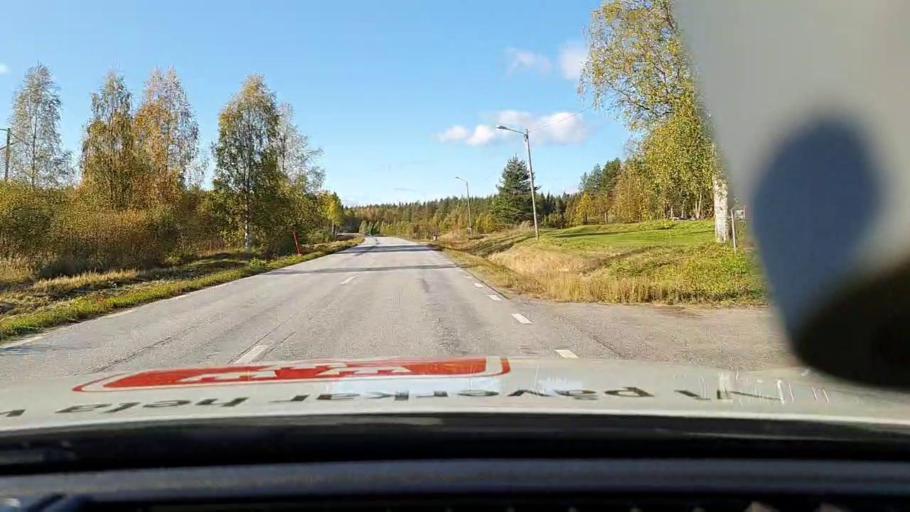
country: SE
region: Norrbotten
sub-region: Pitea Kommun
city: Norrfjarden
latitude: 65.4317
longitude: 21.4887
